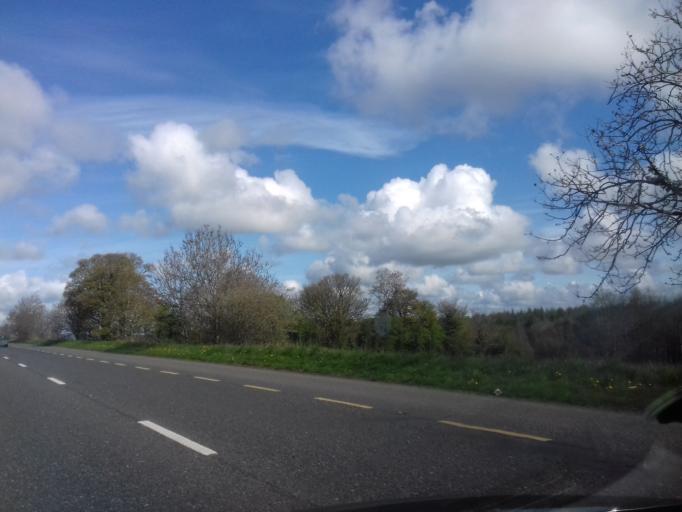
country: IE
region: Ulster
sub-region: An Cabhan
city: Mullagh
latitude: 53.7802
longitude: -7.0097
